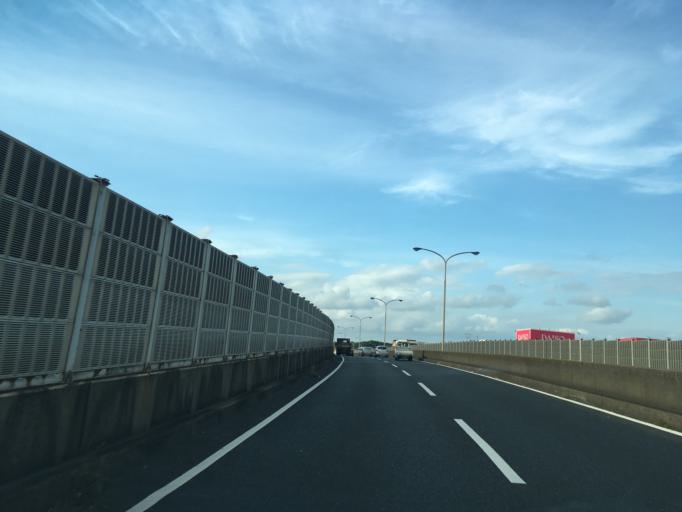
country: JP
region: Chiba
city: Kisarazu
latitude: 35.3767
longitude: 139.9413
